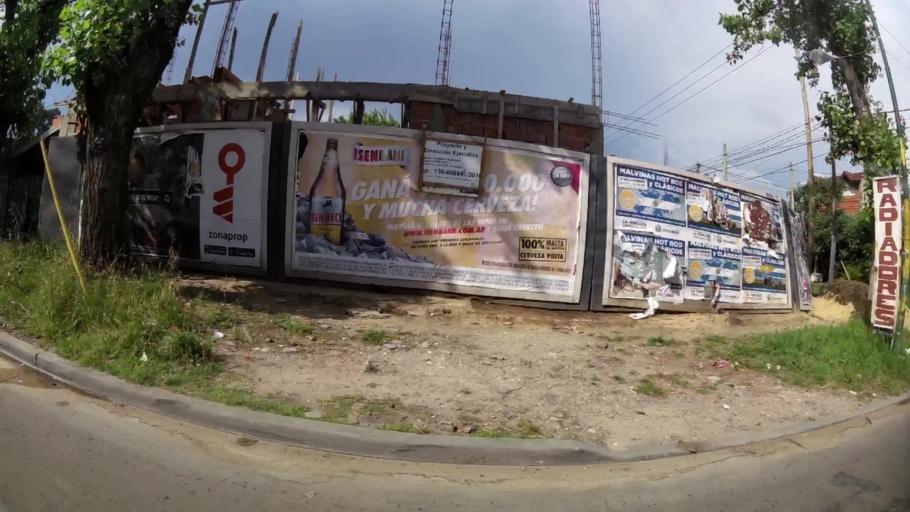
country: AR
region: Buenos Aires
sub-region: Partido de Merlo
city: Merlo
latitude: -34.6371
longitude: -58.7013
